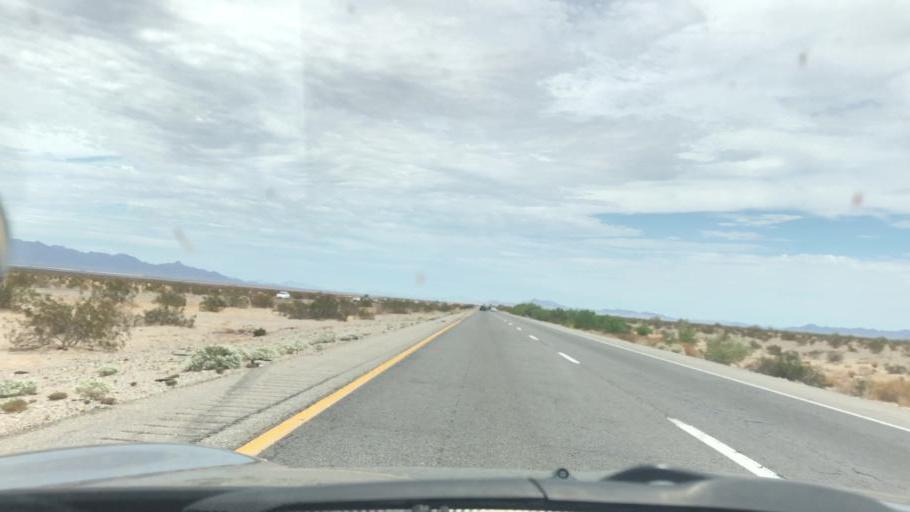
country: US
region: California
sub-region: Riverside County
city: Mesa Verde
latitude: 33.6482
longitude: -115.1285
